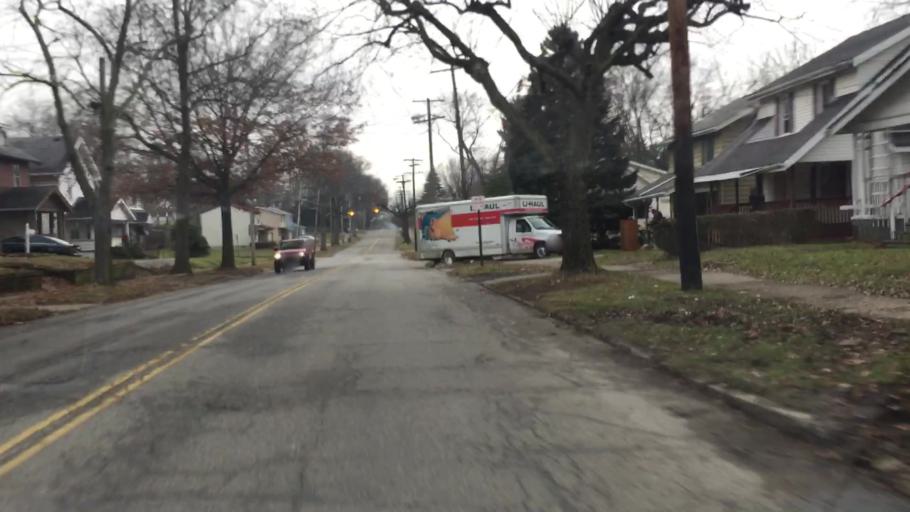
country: US
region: Ohio
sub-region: Summit County
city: Tallmadge
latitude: 41.0801
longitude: -81.4735
